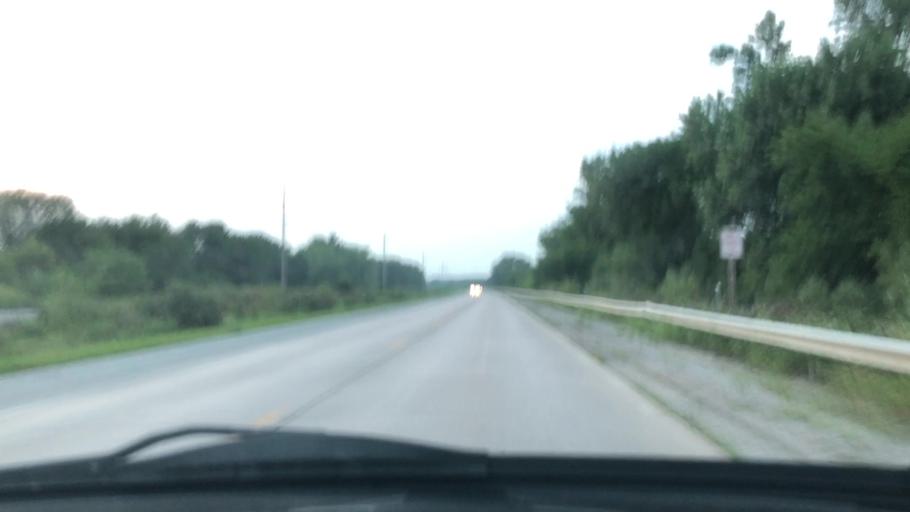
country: US
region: Iowa
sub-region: Johnson County
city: North Liberty
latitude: 41.7897
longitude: -91.6383
